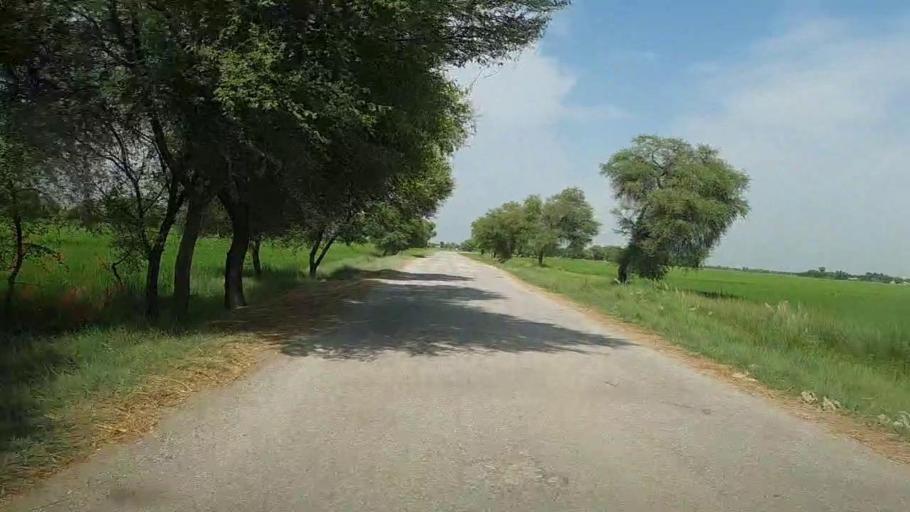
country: PK
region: Sindh
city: Thul
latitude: 28.2339
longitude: 68.7974
